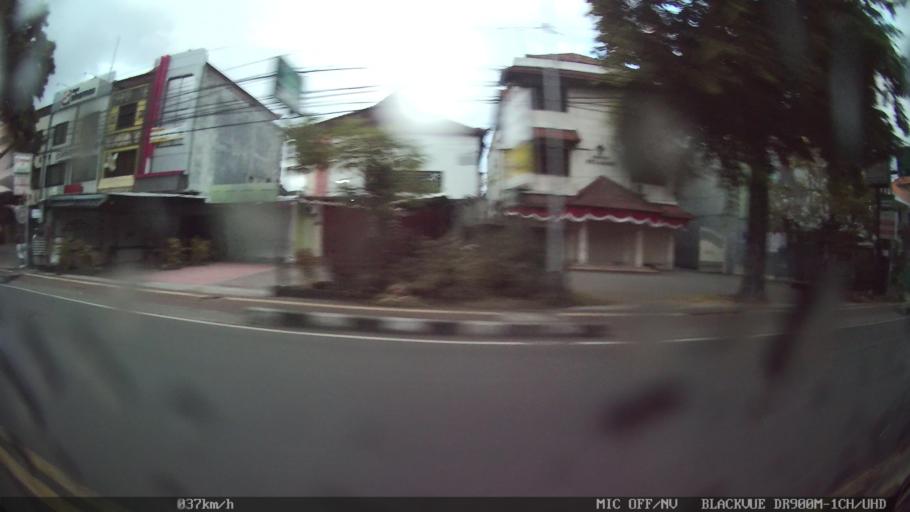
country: ID
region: Bali
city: Banjar Kayangan
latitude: -8.6353
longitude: 115.2242
